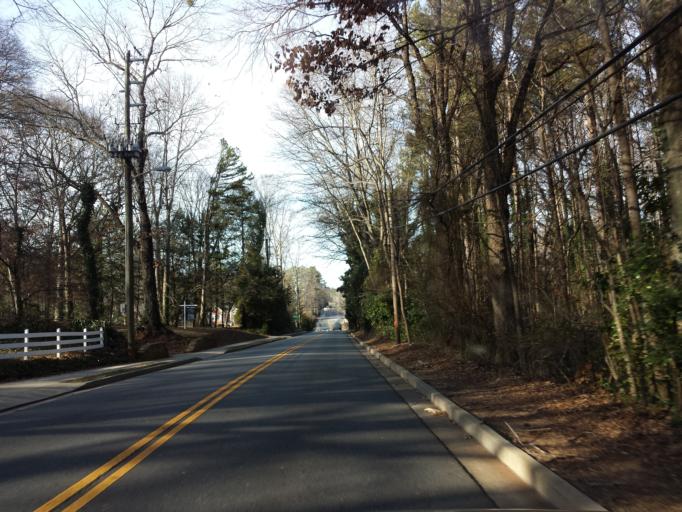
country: US
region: Georgia
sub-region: Cobb County
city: Marietta
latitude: 33.9669
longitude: -84.5616
